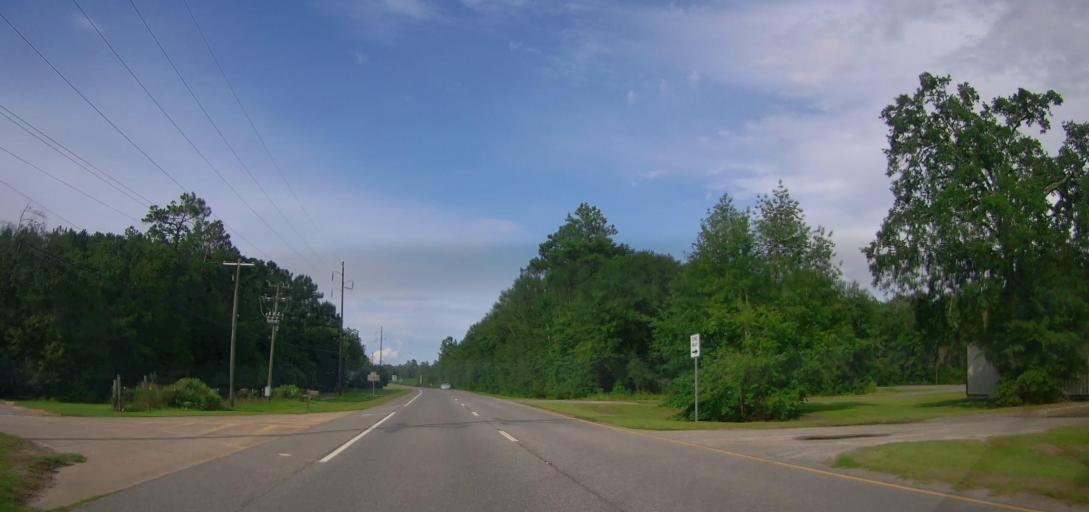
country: US
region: Georgia
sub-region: Wayne County
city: Jesup
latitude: 31.4951
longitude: -82.0075
